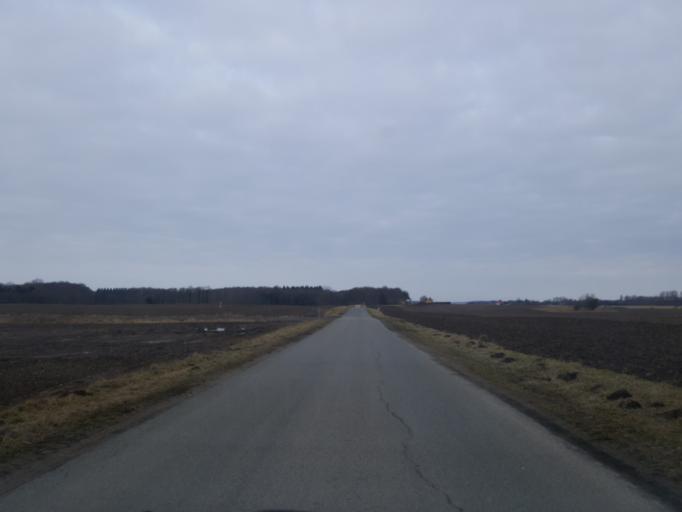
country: DK
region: Zealand
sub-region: Vordingborg Kommune
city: Neder Vindinge
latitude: 55.0289
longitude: 11.8537
